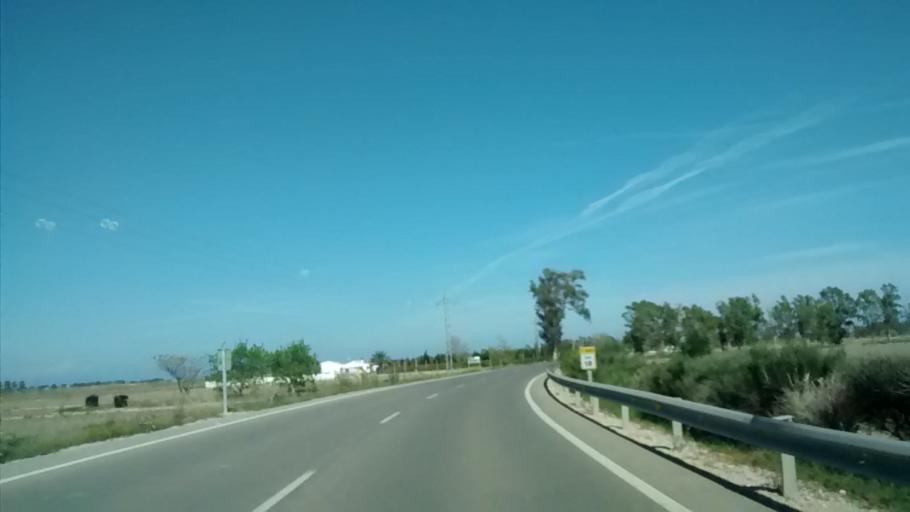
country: ES
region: Catalonia
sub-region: Provincia de Tarragona
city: Deltebre
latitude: 40.7118
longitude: 0.8189
